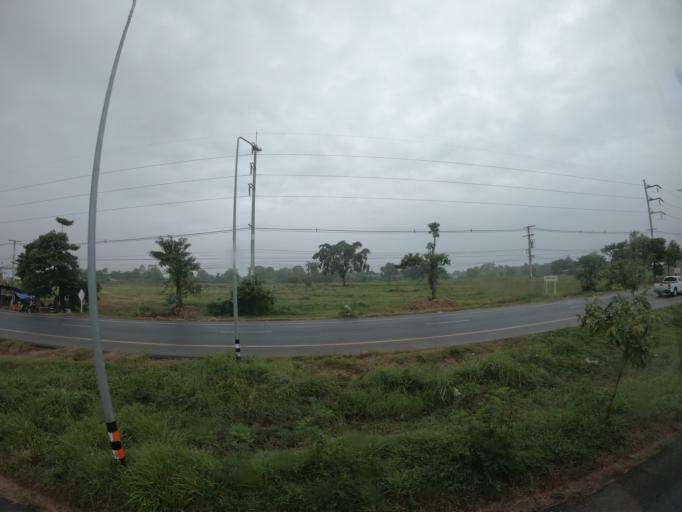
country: TH
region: Maha Sarakham
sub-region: Amphoe Borabue
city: Borabue
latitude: 16.0494
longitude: 103.0958
